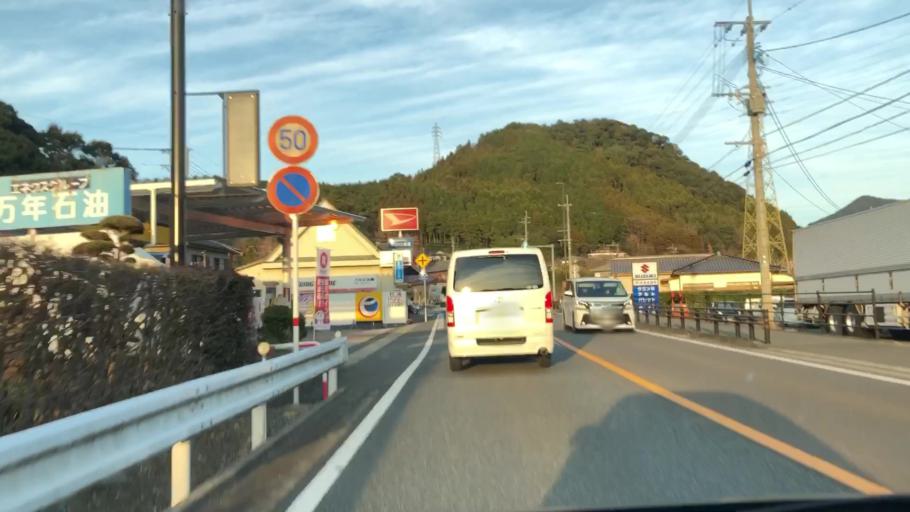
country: JP
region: Kumamoto
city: Minamata
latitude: 32.2336
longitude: 130.4642
